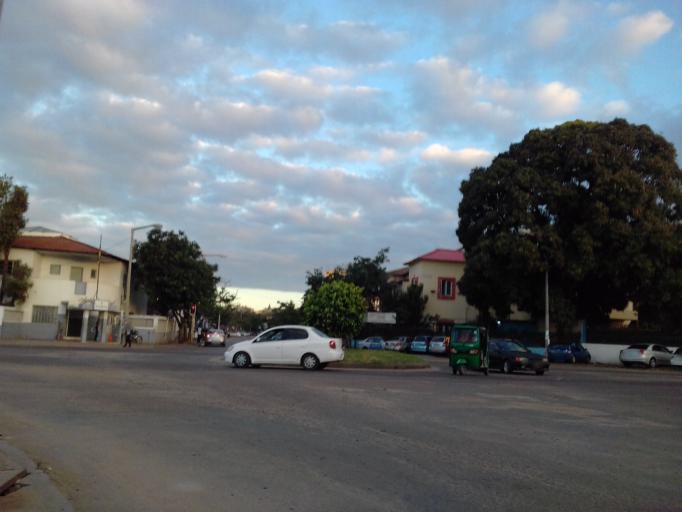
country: MZ
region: Maputo City
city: Maputo
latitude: -25.9568
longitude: 32.5755
